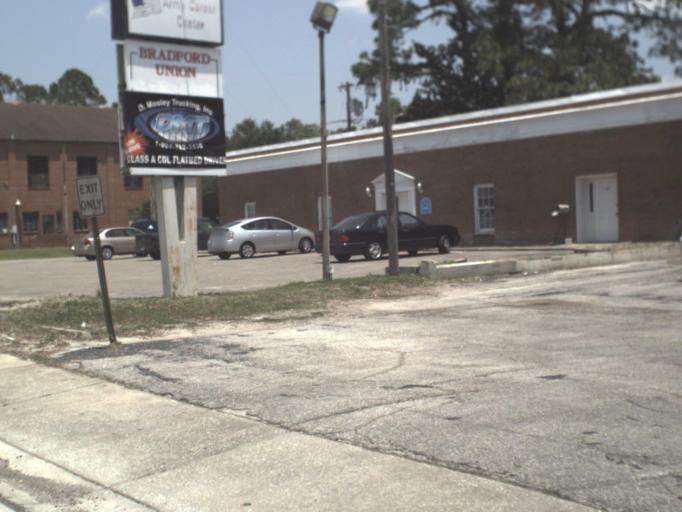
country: US
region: Florida
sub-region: Bradford County
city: Starke
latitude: 29.9485
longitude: -82.1099
